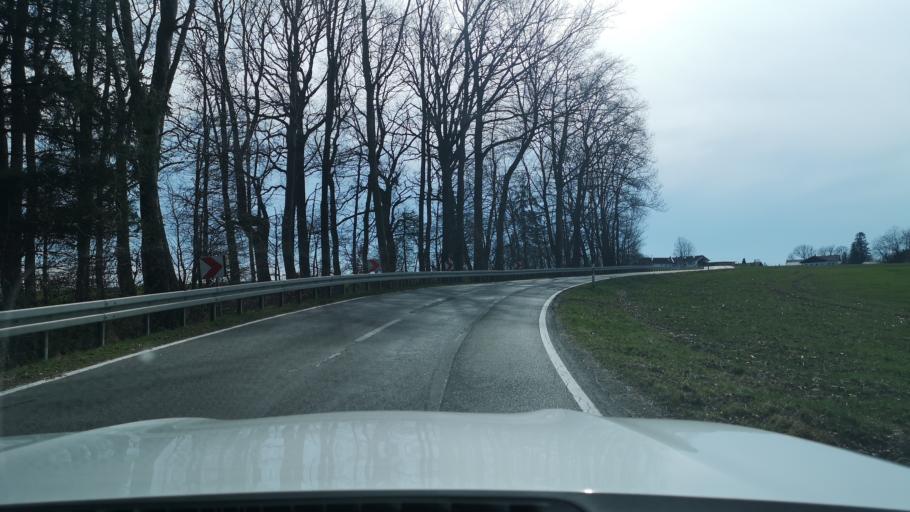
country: DE
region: Bavaria
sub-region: Upper Bavaria
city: Hohenlinden
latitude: 48.1728
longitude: 12.0357
